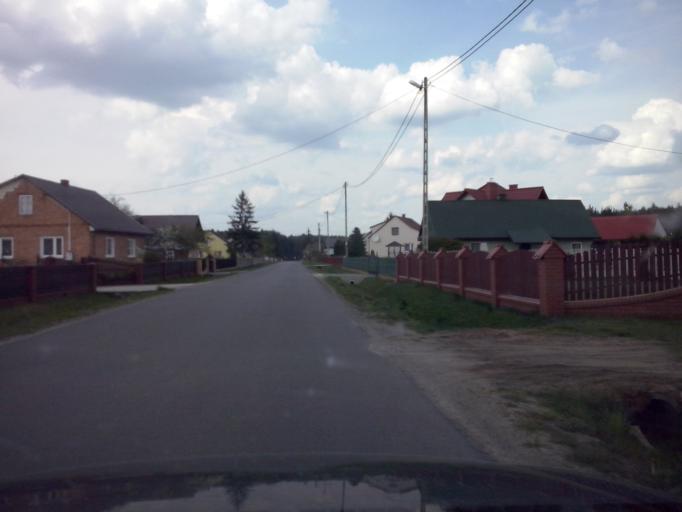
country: PL
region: Subcarpathian Voivodeship
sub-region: Powiat lezajski
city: Letownia
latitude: 50.3531
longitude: 22.2052
